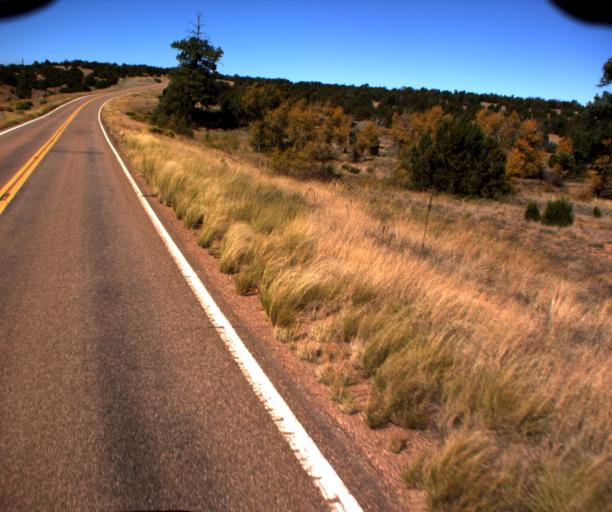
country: US
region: Arizona
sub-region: Navajo County
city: Heber-Overgaard
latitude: 34.4529
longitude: -110.4581
